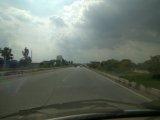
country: IN
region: Karnataka
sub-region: Kolar
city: Kolar
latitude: 13.1285
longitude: 77.9947
